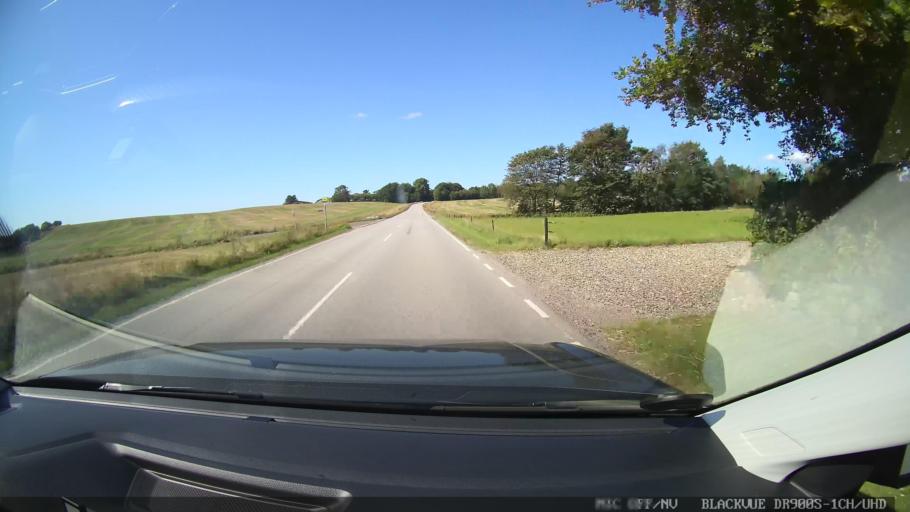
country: DK
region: North Denmark
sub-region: Mariagerfjord Kommune
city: Mariager
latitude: 56.6204
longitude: 9.9811
